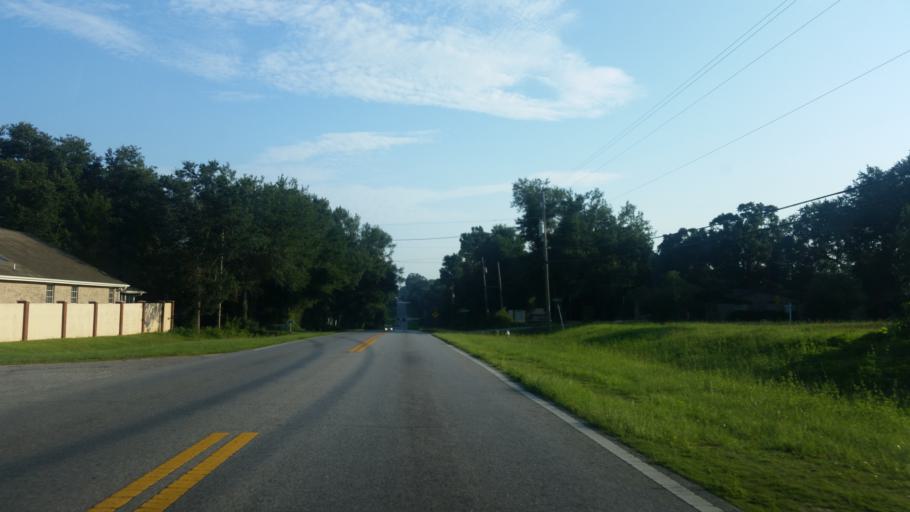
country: US
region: Florida
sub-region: Escambia County
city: Ensley
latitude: 30.5562
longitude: -87.2616
